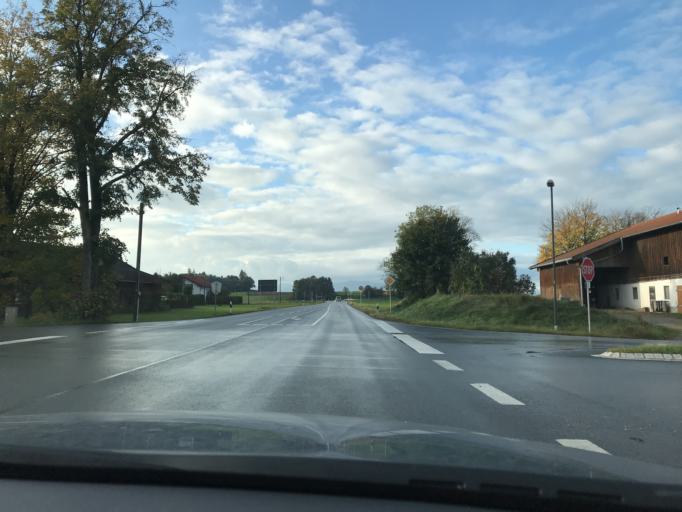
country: DE
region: Bavaria
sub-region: Upper Bavaria
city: Egling
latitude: 47.8871
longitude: 11.5056
